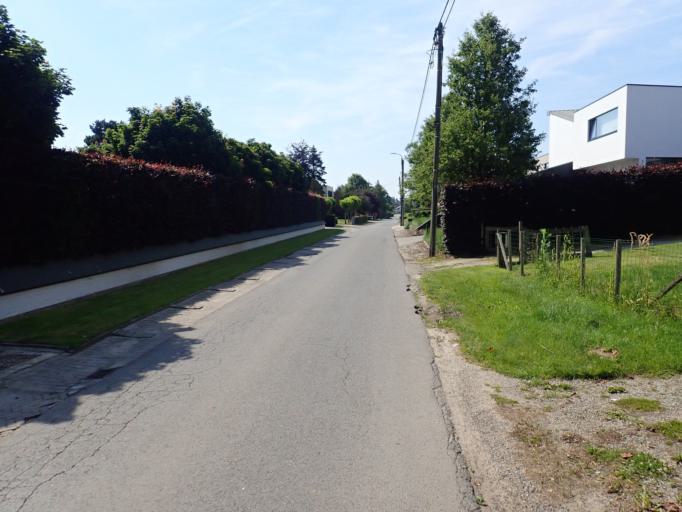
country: BE
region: Flanders
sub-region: Provincie Oost-Vlaanderen
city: Temse
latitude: 51.1391
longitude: 4.2255
